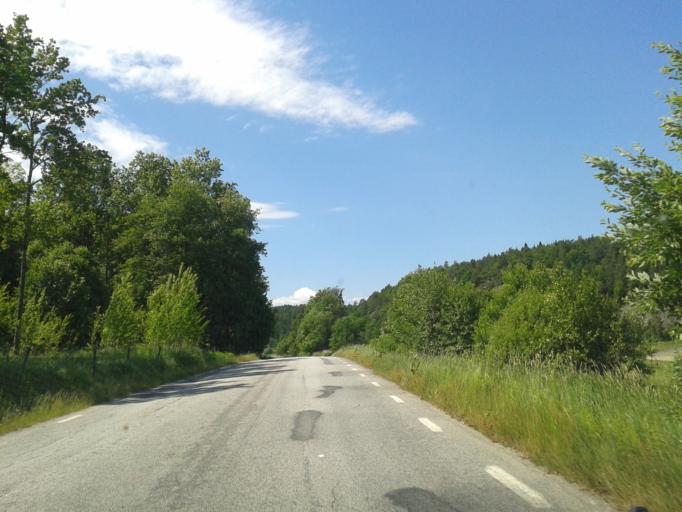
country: SE
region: Vaestra Goetaland
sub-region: Uddevalla Kommun
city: Ljungskile
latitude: 58.2837
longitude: 11.9082
